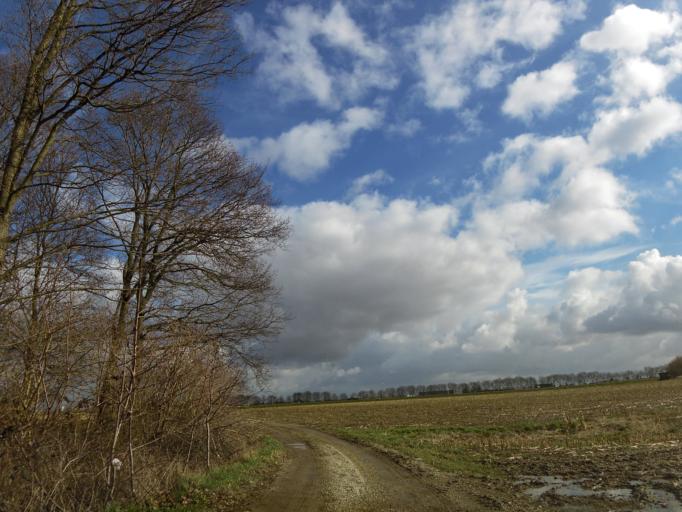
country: NL
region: Limburg
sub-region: Gemeente Sittard-Geleen
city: Born
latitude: 51.0411
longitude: 5.7959
